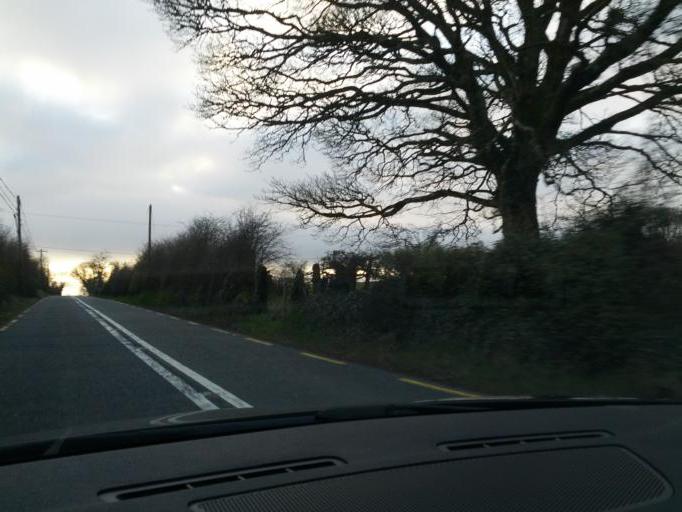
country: IE
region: Connaught
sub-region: Sligo
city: Ballymote
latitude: 54.1283
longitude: -8.5724
